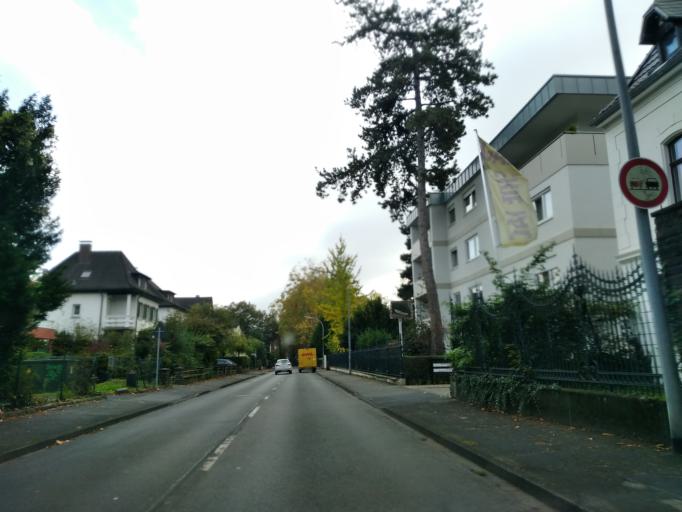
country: DE
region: North Rhine-Westphalia
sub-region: Regierungsbezirk Koln
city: Konigswinter
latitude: 50.6812
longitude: 7.1875
